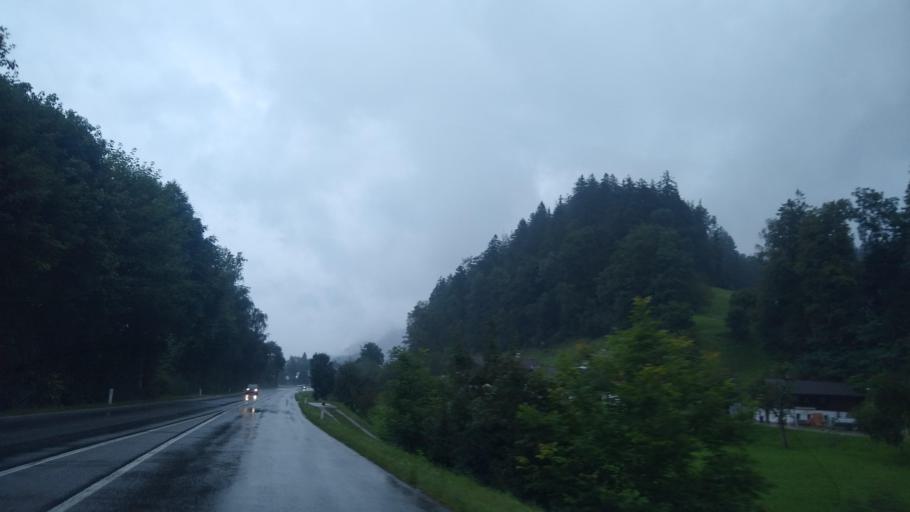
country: AT
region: Tyrol
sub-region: Politischer Bezirk Kufstein
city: Munster
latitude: 47.4116
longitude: 11.8496
